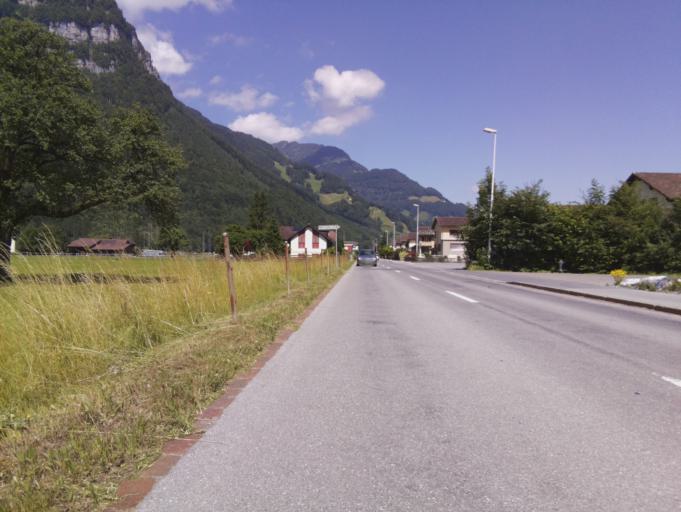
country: CH
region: Glarus
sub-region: Glarus
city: Nafels
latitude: 47.1023
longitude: 9.0691
